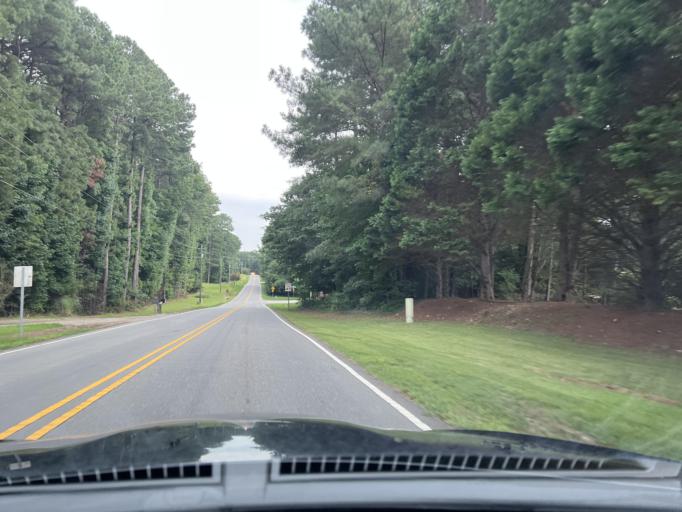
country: US
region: North Carolina
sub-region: Wake County
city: Wake Forest
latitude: 36.0110
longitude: -78.5411
